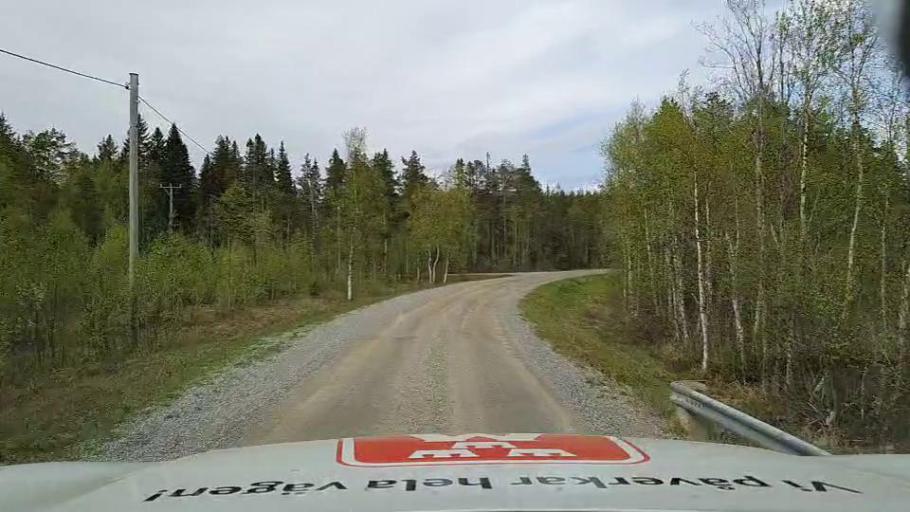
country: SE
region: Jaemtland
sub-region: OEstersunds Kommun
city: Brunflo
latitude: 62.5955
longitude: 14.9144
